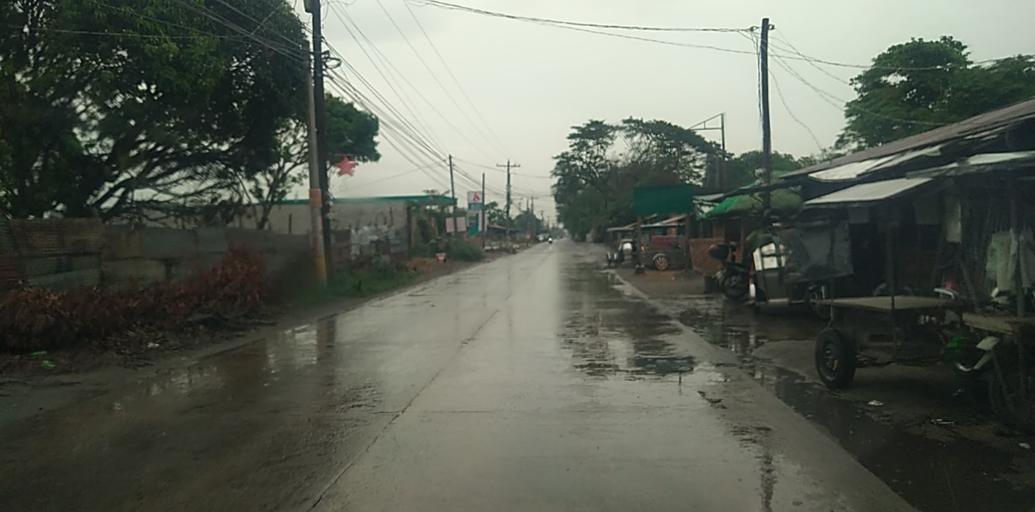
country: PH
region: Central Luzon
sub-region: Province of Pampanga
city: San Antonio
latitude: 15.1597
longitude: 120.6858
